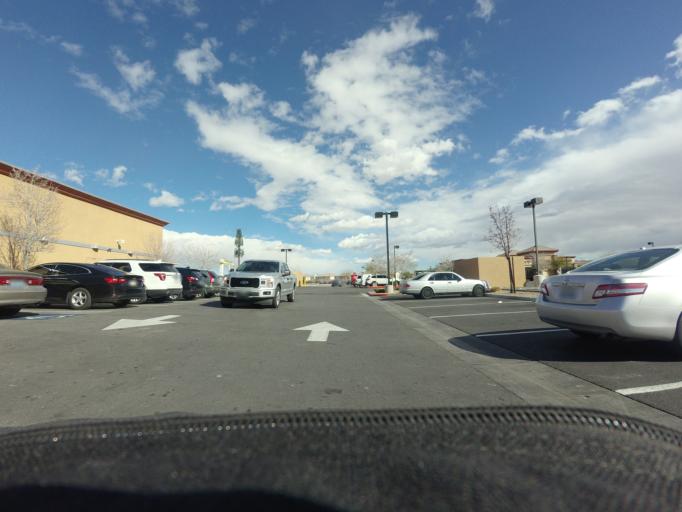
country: US
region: Nevada
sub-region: Clark County
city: Nellis Air Force Base
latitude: 36.2646
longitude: -115.1166
